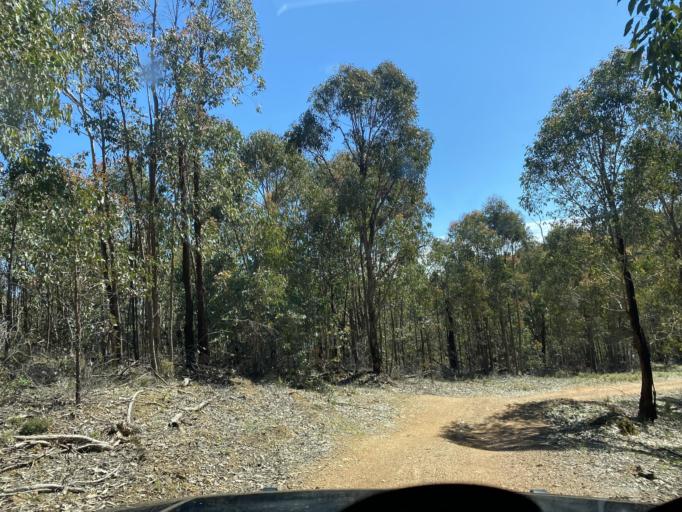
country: AU
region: Victoria
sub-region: Benalla
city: Benalla
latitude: -36.7286
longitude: 146.1815
